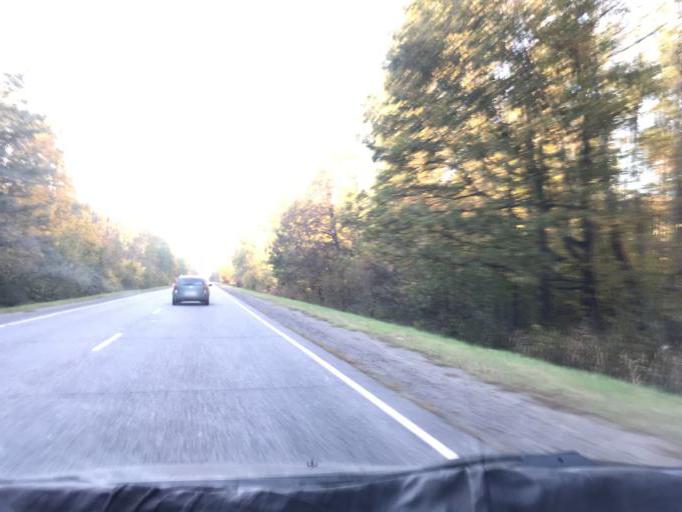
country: BY
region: Gomel
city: Pyetrykaw
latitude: 52.2631
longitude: 28.3154
